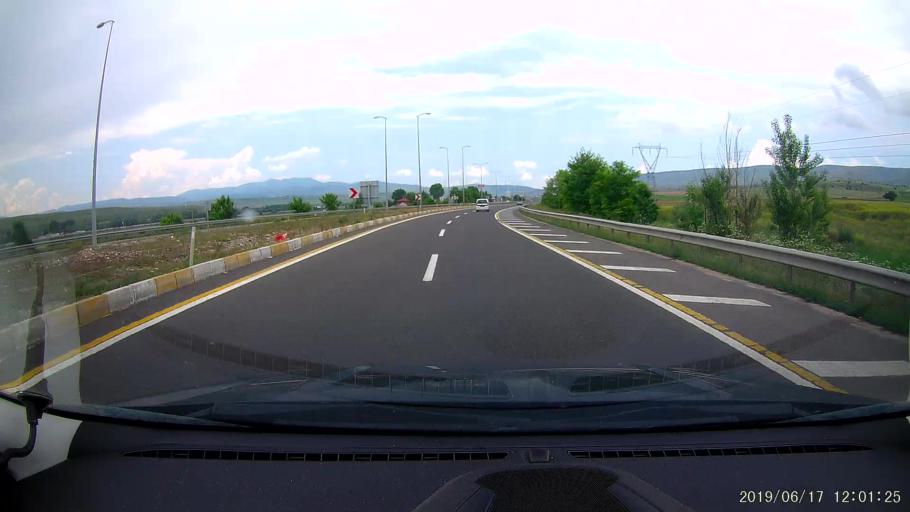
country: TR
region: Cankiri
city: Cerkes
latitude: 40.8215
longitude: 32.8689
